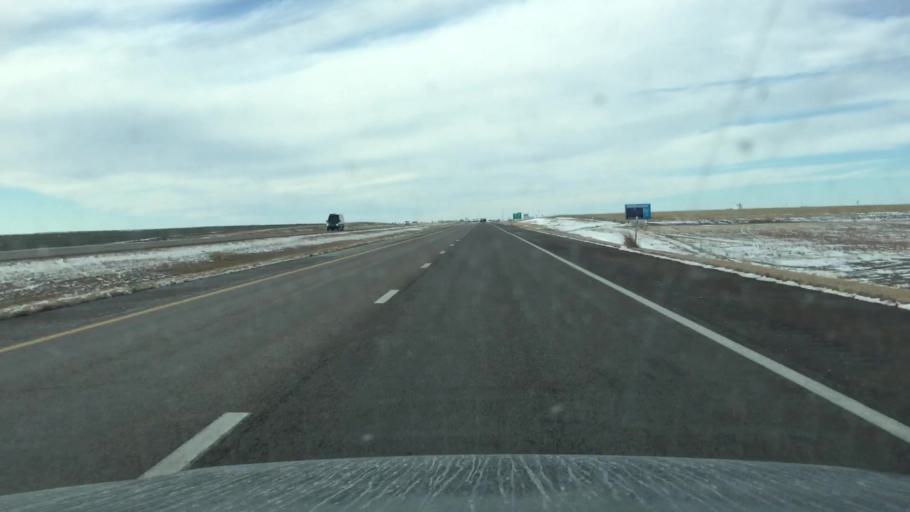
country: US
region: Kansas
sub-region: Trego County
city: WaKeeney
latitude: 39.0060
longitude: -99.8441
